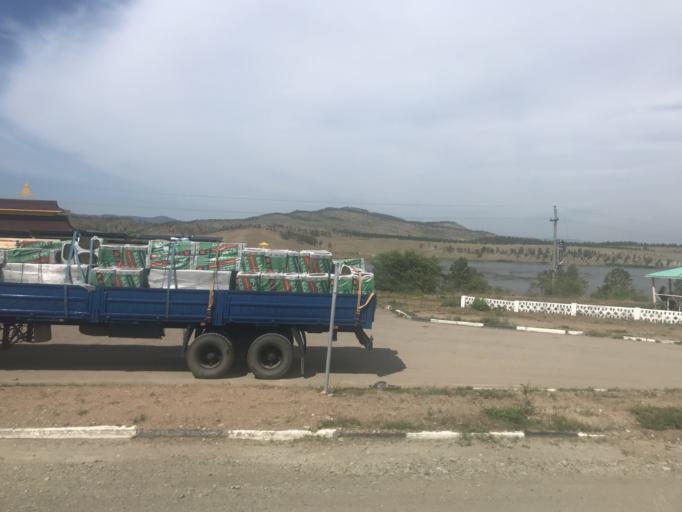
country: RU
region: Respublika Buryatiya
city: Gusinoozyorsk
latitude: 51.4795
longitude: 106.7569
